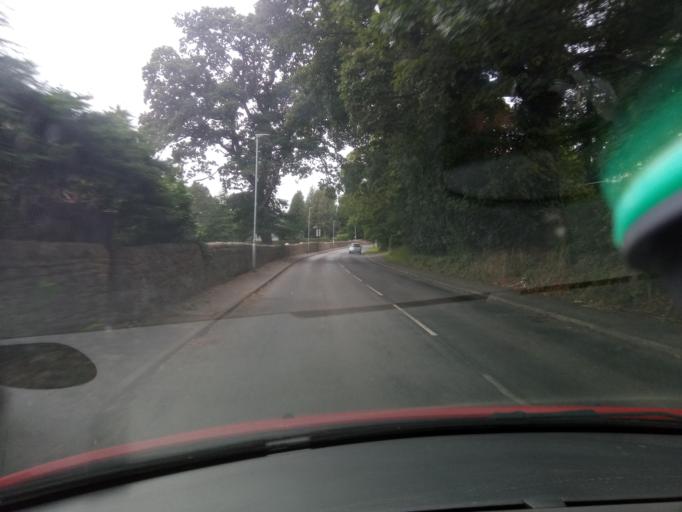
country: GB
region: England
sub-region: Northumberland
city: Hexham
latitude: 54.9693
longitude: -2.1213
